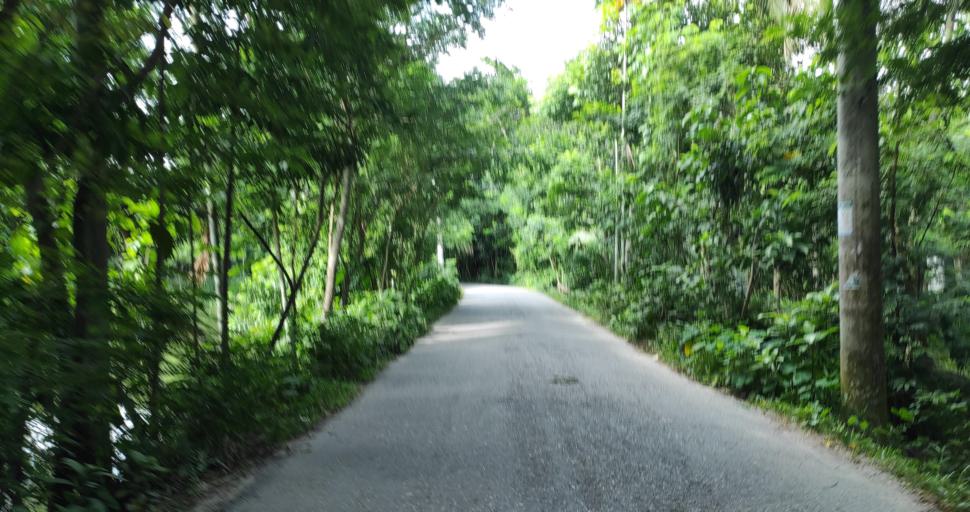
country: BD
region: Barisal
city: Gaurnadi
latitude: 22.8946
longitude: 90.1863
